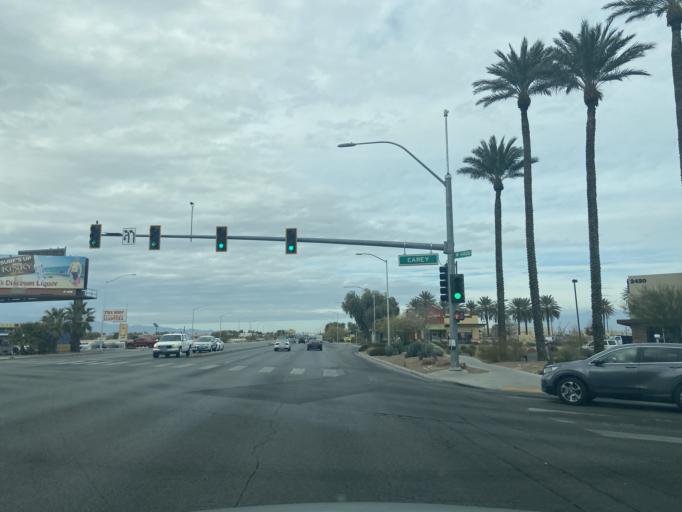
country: US
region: Nevada
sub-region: Clark County
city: Las Vegas
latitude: 36.2027
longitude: -115.1988
